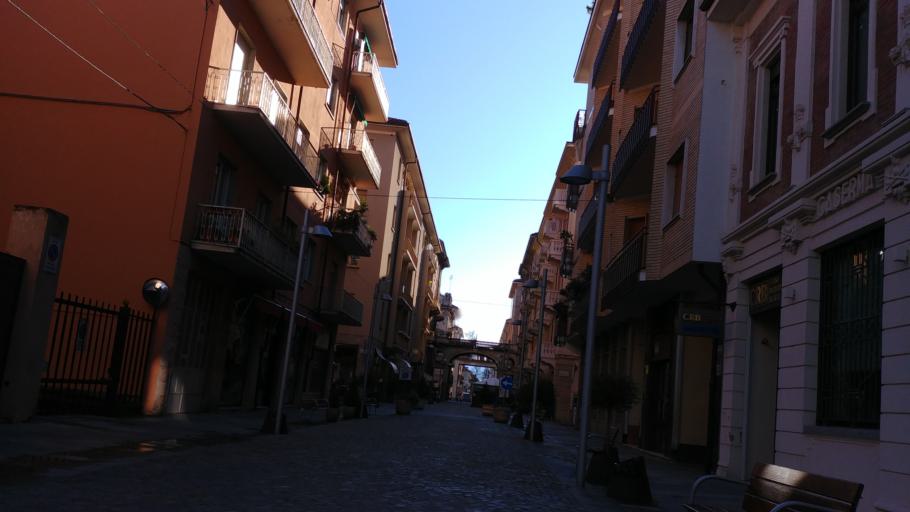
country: IT
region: Piedmont
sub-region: Provincia di Cuneo
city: Cuneo
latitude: 44.3872
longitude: 7.5437
